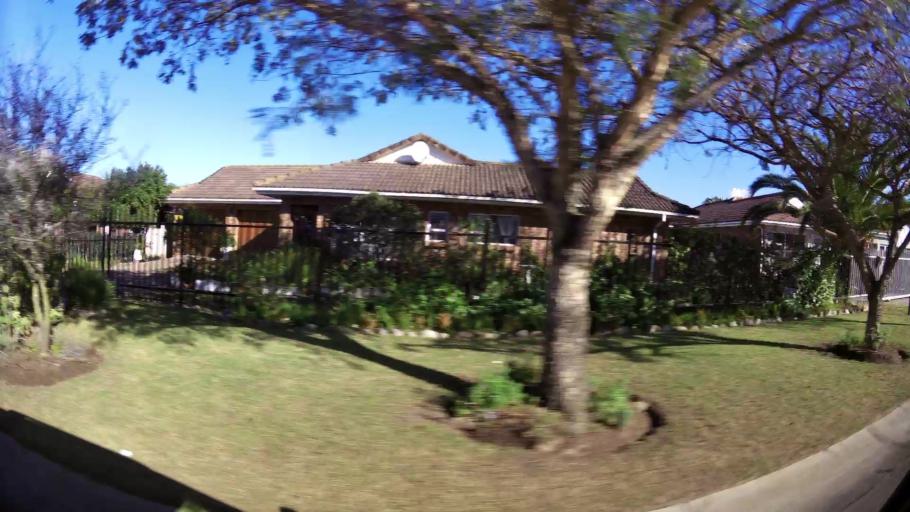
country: ZA
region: Western Cape
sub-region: Eden District Municipality
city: George
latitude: -33.9598
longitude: 22.4244
